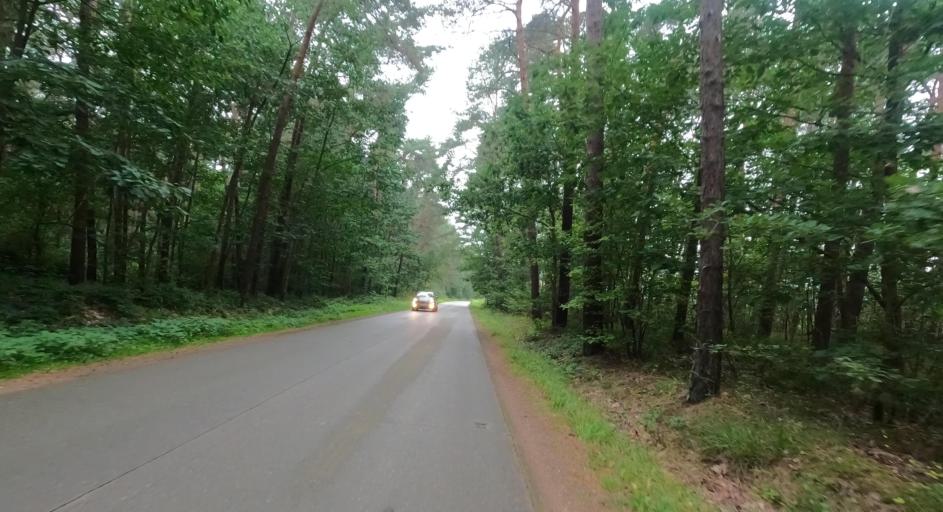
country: BE
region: Flanders
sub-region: Provincie Antwerpen
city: Vorselaar
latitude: 51.2165
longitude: 4.7916
